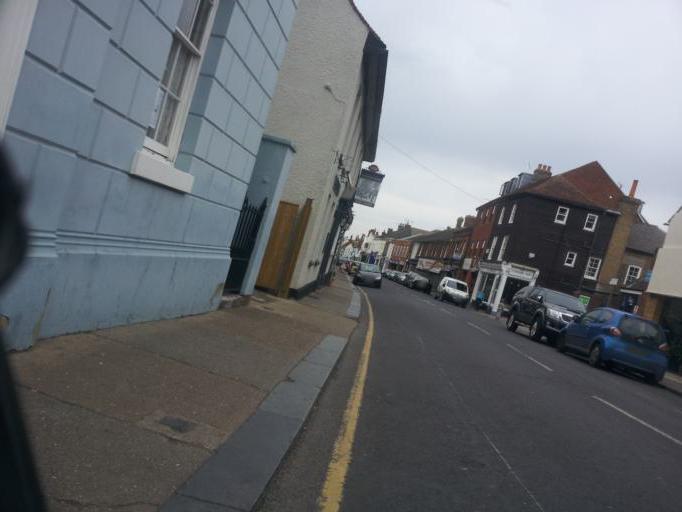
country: GB
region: England
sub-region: Kent
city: Faversham
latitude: 51.3127
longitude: 0.8902
